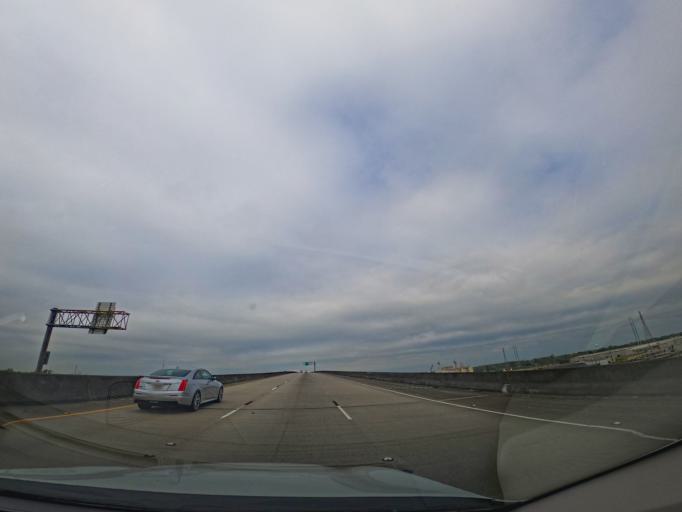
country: US
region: Louisiana
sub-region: Saint Mary Parish
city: Amelia
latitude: 29.6704
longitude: -91.0942
